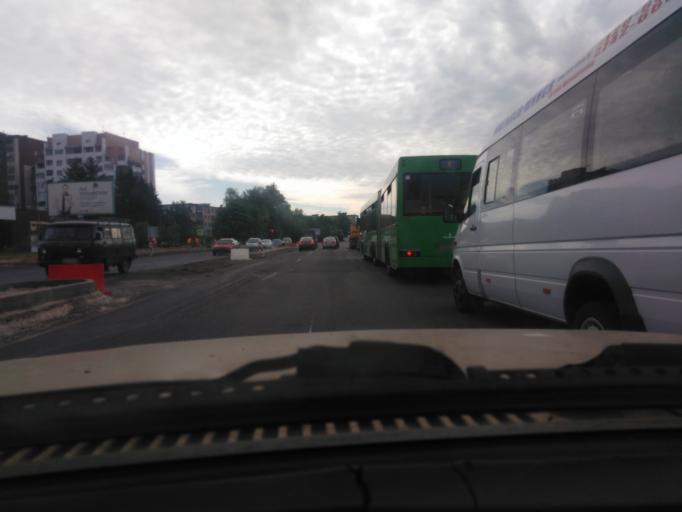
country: BY
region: Mogilev
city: Mahilyow
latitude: 53.9190
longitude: 30.3012
